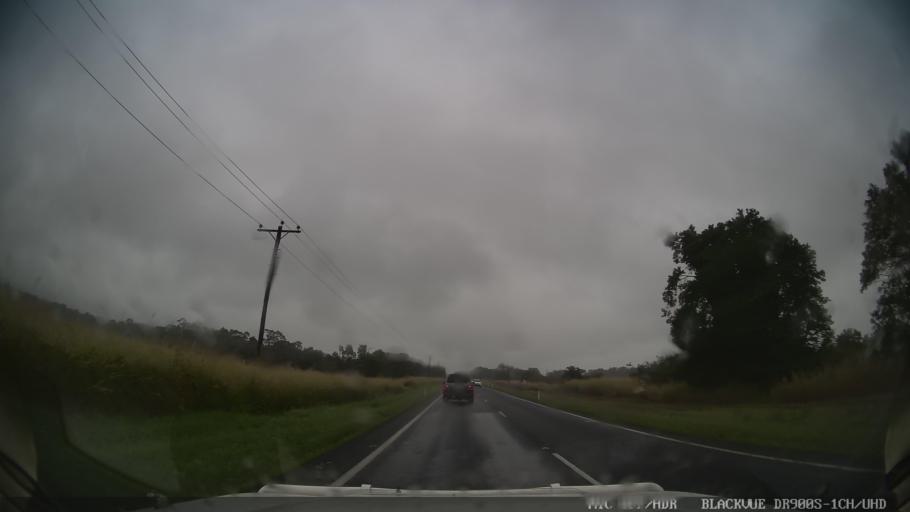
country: AU
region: Queensland
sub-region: Cassowary Coast
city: Innisfail
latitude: -17.6540
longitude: 146.0351
